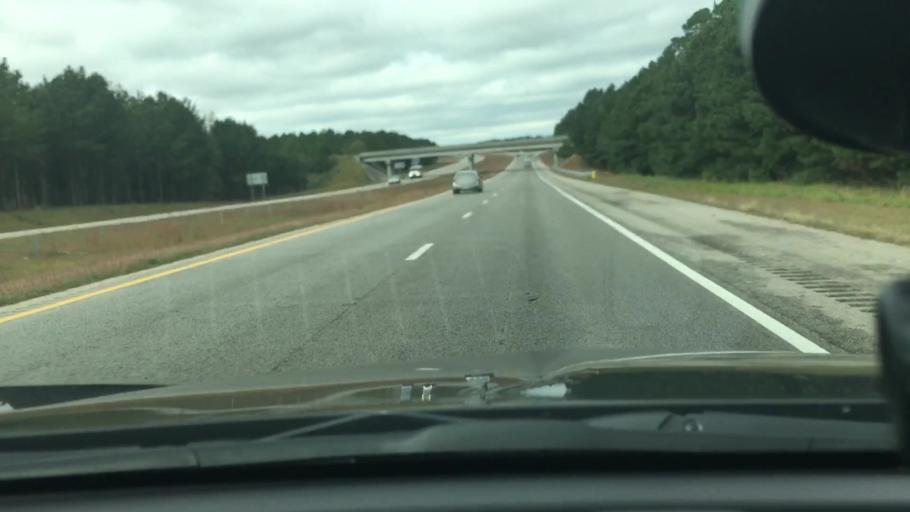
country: US
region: North Carolina
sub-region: Wilson County
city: Lucama
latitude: 35.7253
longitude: -78.0073
